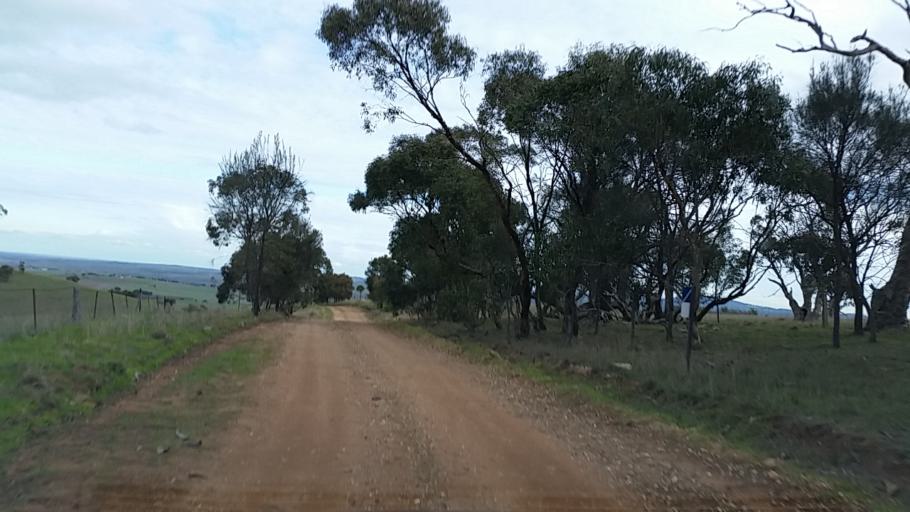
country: AU
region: South Australia
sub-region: Mount Barker
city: Callington
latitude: -34.9987
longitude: 139.0552
